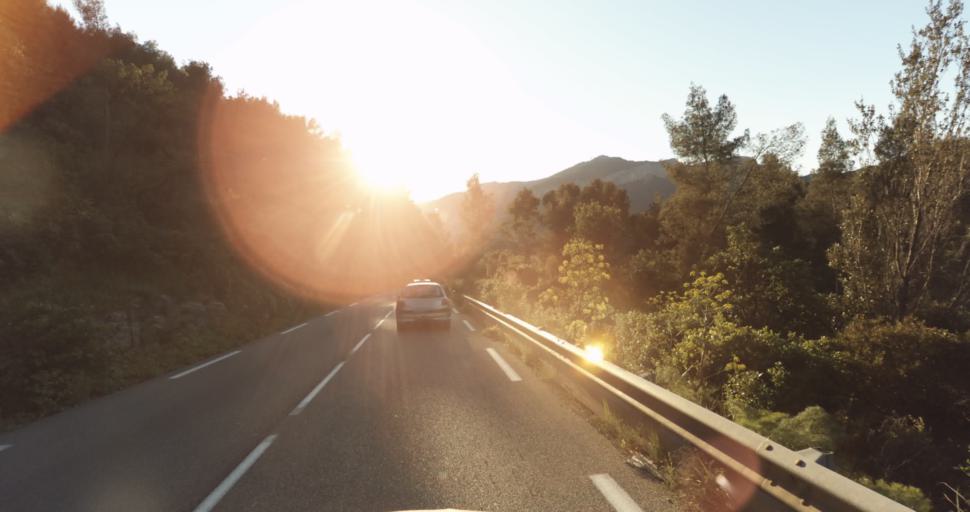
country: FR
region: Provence-Alpes-Cote d'Azur
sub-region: Departement du Var
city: Le Revest-les-Eaux
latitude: 43.1635
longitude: 5.9442
